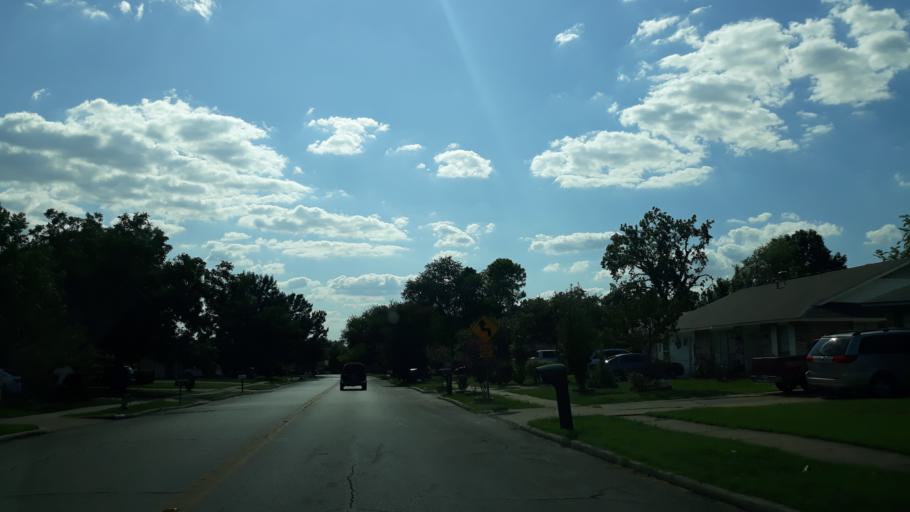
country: US
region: Texas
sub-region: Dallas County
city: Irving
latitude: 32.8513
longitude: -96.9969
